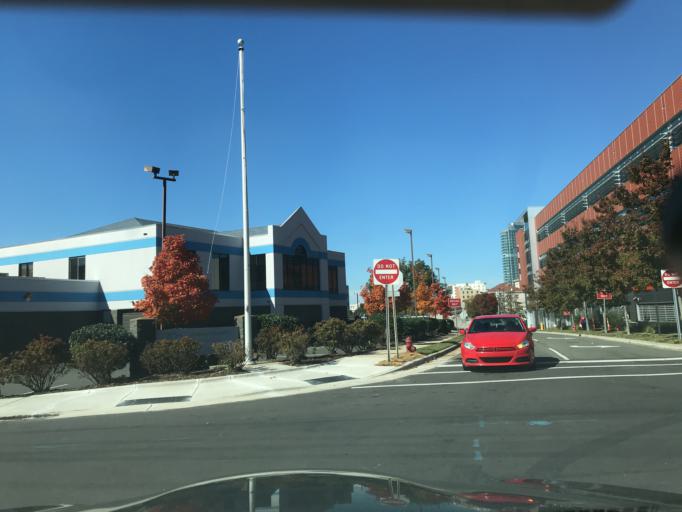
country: US
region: North Carolina
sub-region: Durham County
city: Durham
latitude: 35.9910
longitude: -78.8966
